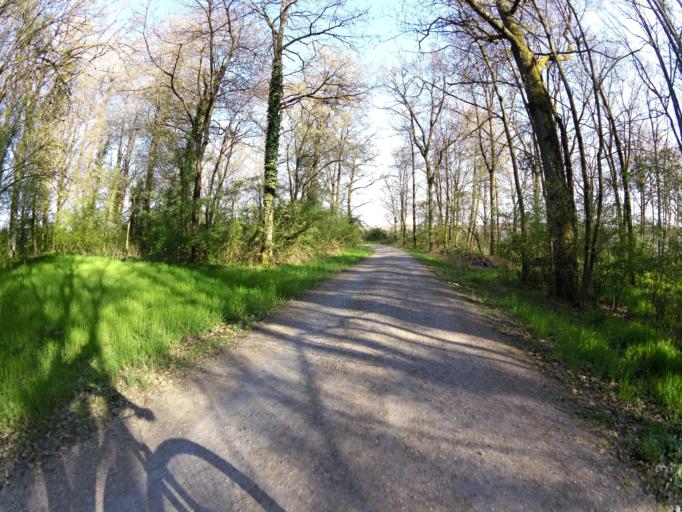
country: DE
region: Bavaria
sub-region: Regierungsbezirk Unterfranken
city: Estenfeld
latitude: 49.8635
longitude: 9.9975
